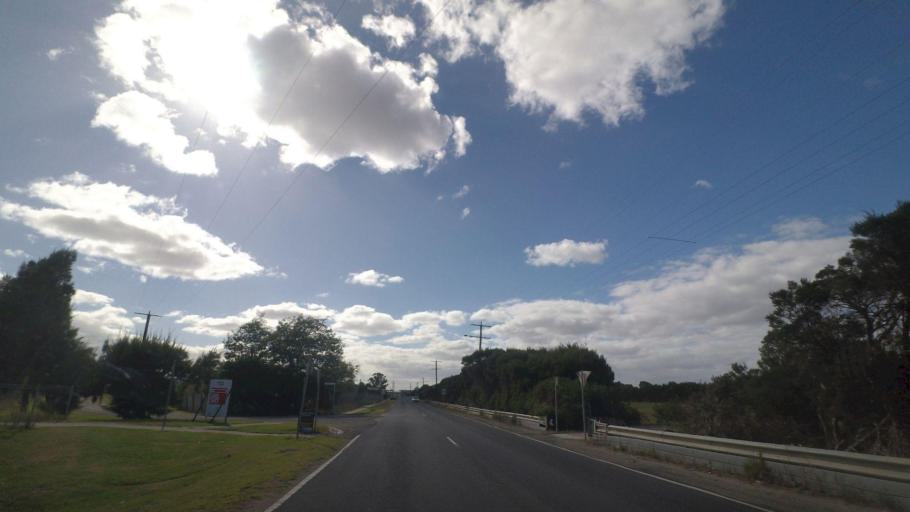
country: AU
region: Victoria
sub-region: Cardinia
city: Koo-Wee-Rup
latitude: -38.1975
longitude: 145.4796
